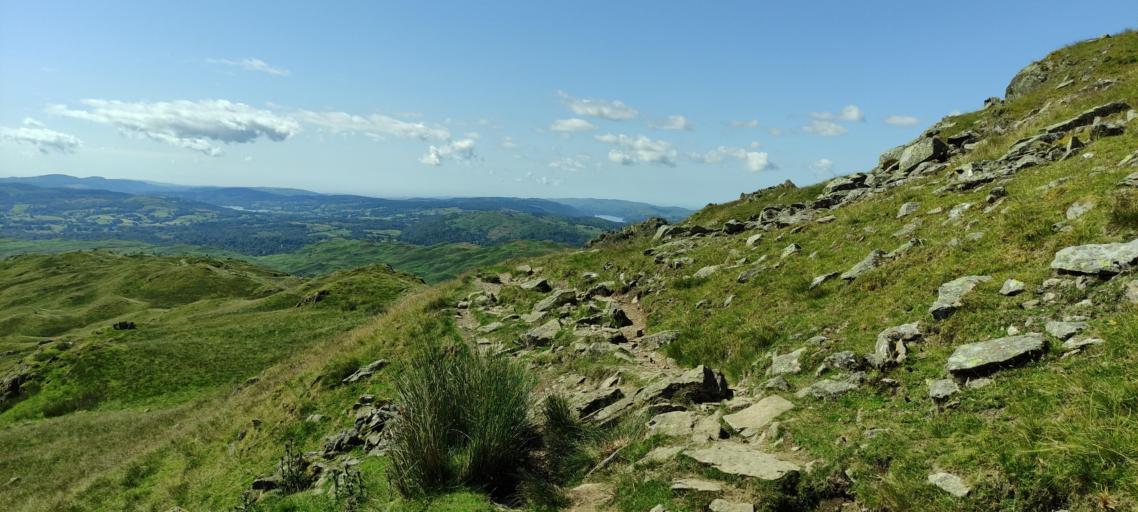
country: GB
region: England
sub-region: Cumbria
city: Ambleside
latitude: 54.4609
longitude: -2.9964
